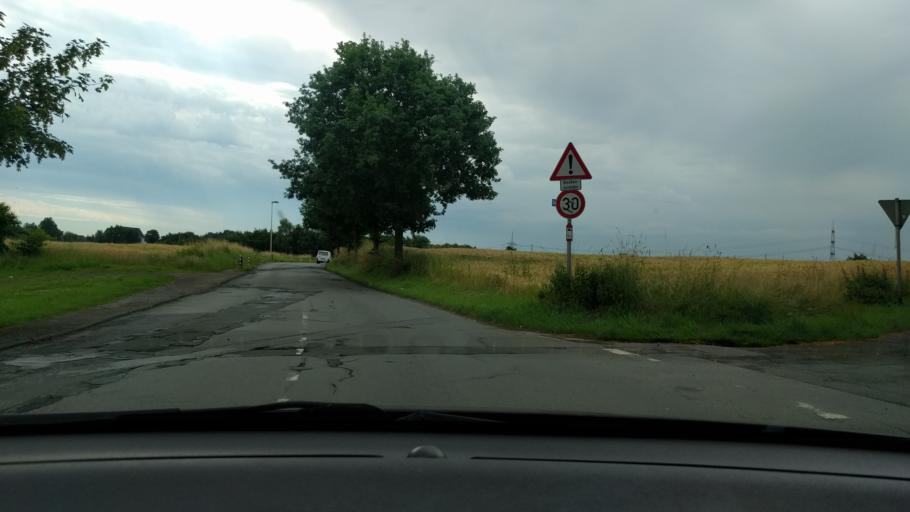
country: DE
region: North Rhine-Westphalia
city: Witten
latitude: 51.4641
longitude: 7.3697
